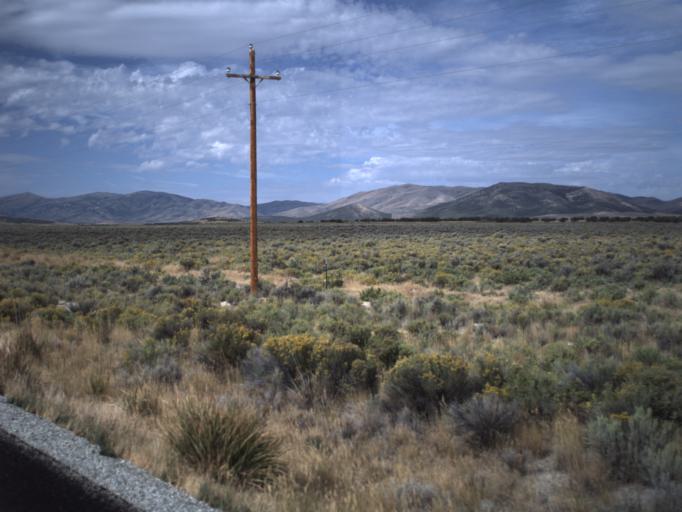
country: US
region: Idaho
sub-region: Cassia County
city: Burley
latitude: 41.7746
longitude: -113.4957
